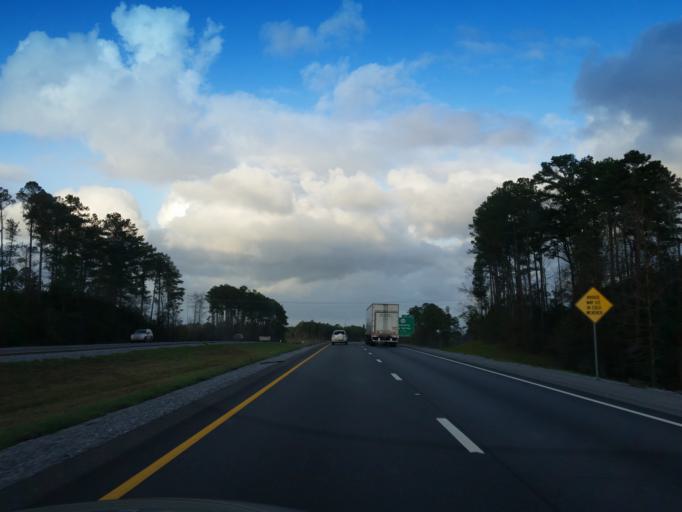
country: US
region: Mississippi
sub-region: Jones County
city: Sharon
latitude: 31.8960
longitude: -89.0298
